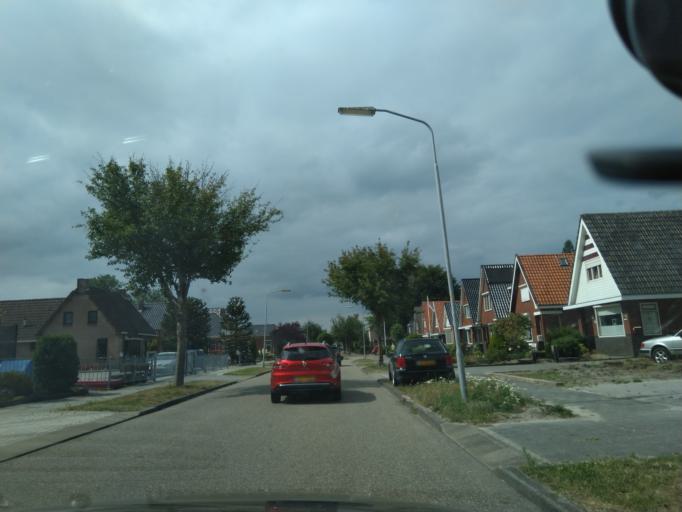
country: NL
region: Groningen
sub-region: Gemeente Pekela
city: Oude Pekela
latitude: 53.0778
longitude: 6.9732
